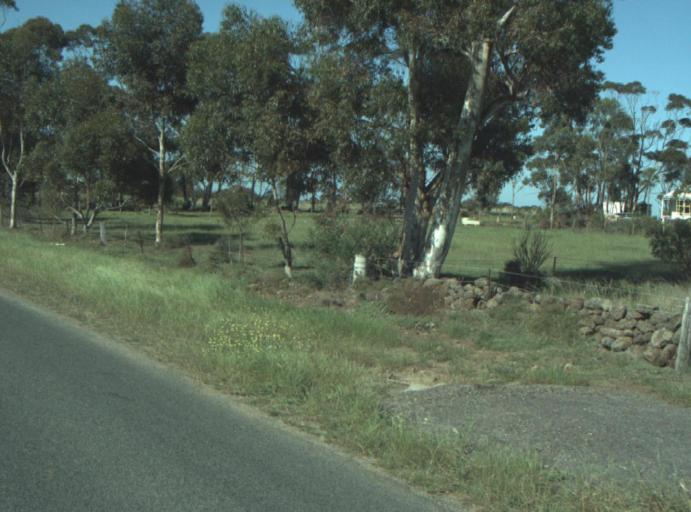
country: AU
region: Victoria
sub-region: Wyndham
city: Little River
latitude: -37.9643
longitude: 144.4628
